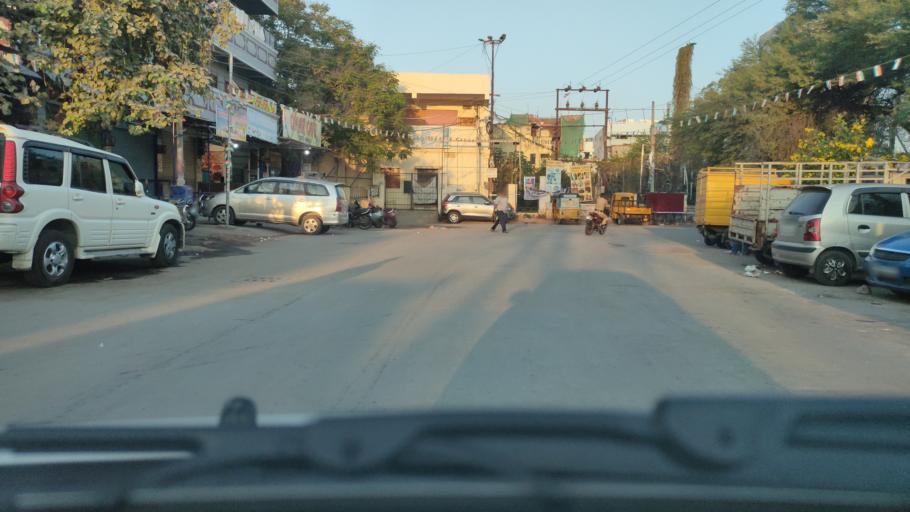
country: IN
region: Telangana
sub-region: Rangareddi
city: Gaddi Annaram
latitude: 17.3866
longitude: 78.5230
